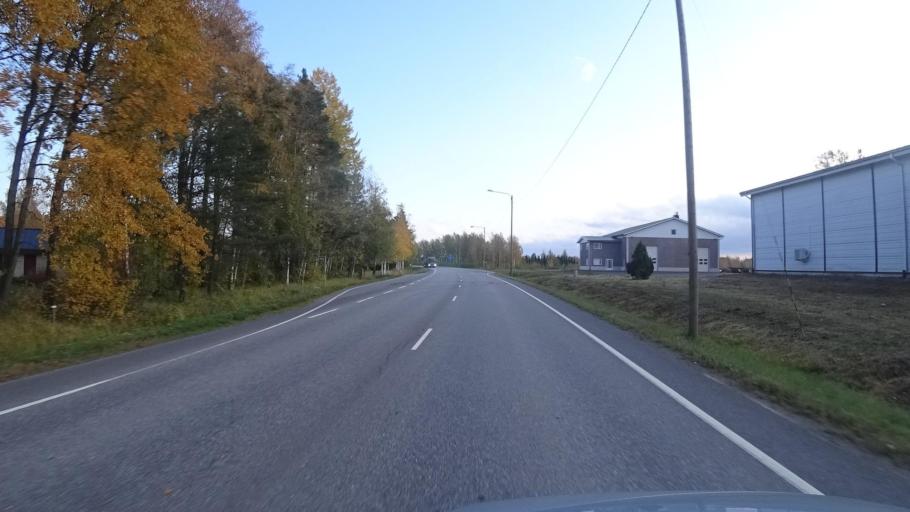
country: FI
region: Satakunta
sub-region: Rauma
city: Saekylae
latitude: 61.0591
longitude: 22.3272
